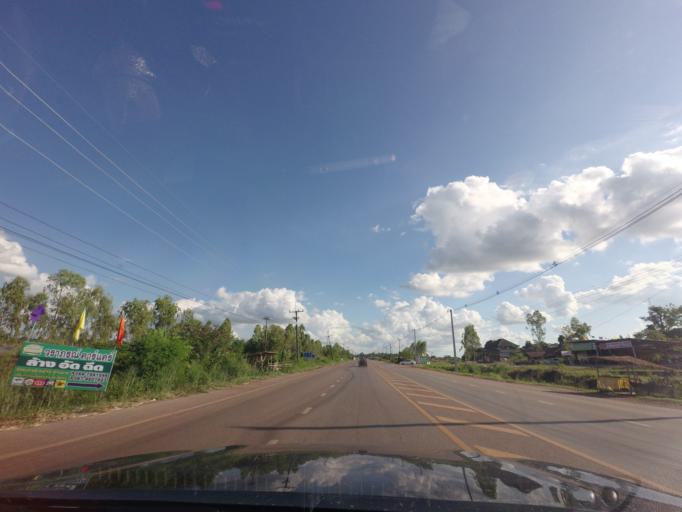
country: TH
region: Changwat Udon Thani
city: Ban Dung
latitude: 17.7174
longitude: 103.2502
